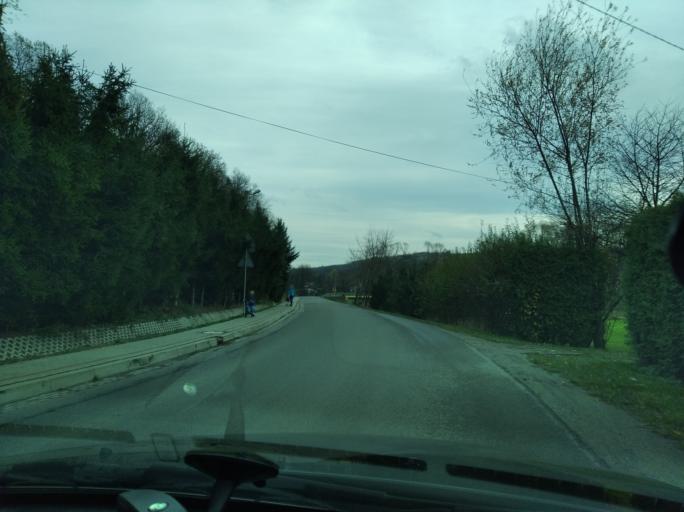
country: PL
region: Subcarpathian Voivodeship
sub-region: Powiat strzyzowski
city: Strzyzow
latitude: 49.9295
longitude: 21.7727
